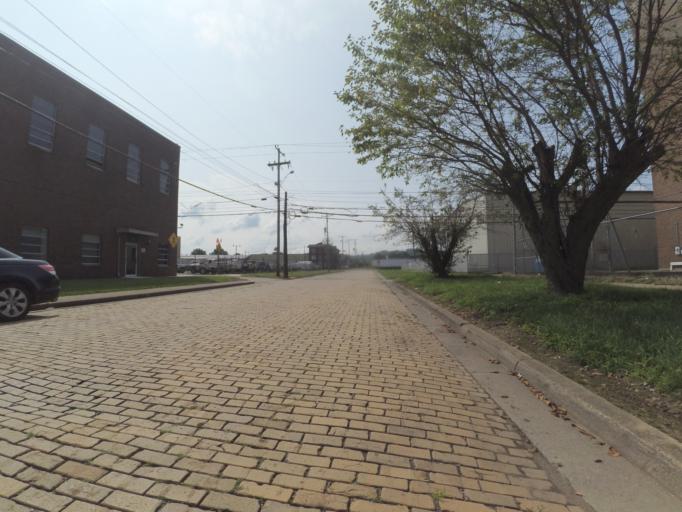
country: US
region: West Virginia
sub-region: Cabell County
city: Huntington
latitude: 38.4185
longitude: -82.4378
